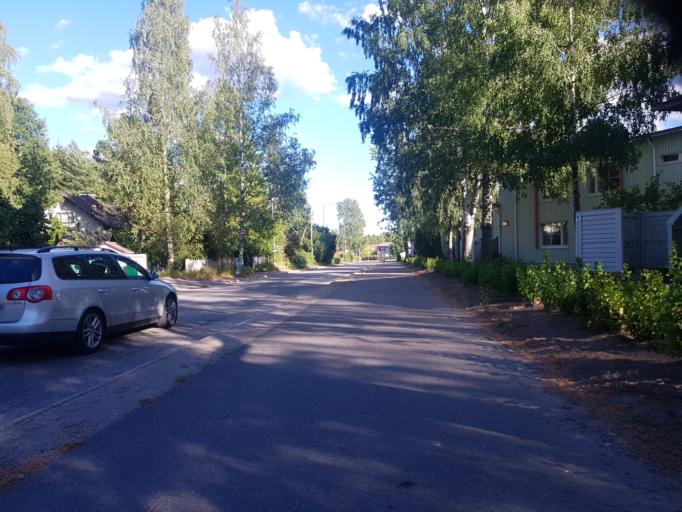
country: FI
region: Uusimaa
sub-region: Helsinki
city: Vantaa
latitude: 60.2702
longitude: 25.0077
